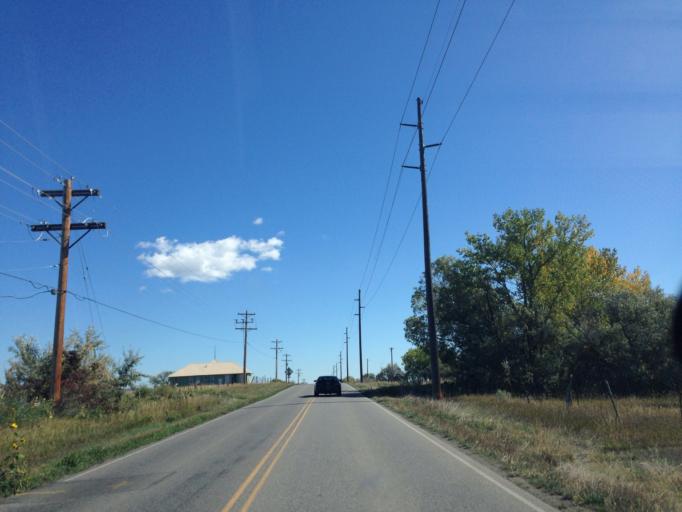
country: US
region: Montana
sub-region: Yellowstone County
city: Laurel
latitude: 45.7840
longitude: -108.6792
